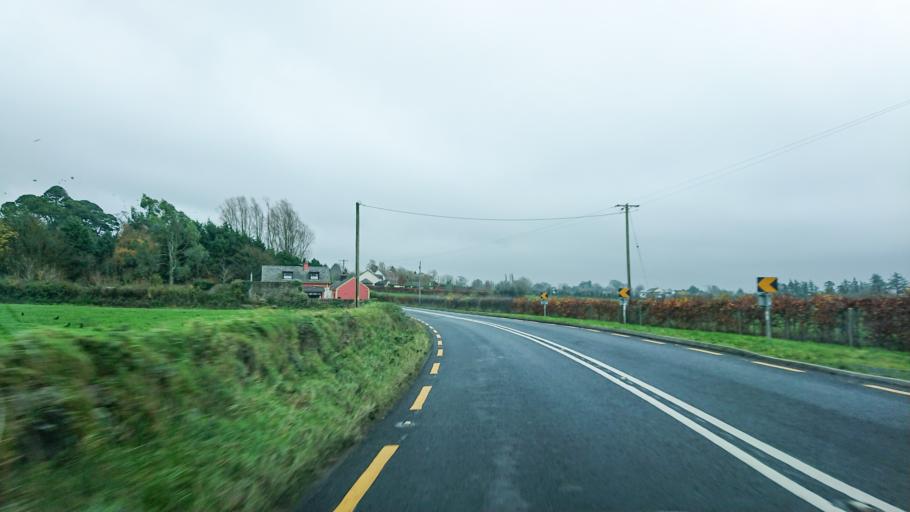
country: IE
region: Leinster
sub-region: Kilkenny
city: Mooncoin
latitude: 52.2990
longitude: -7.2671
